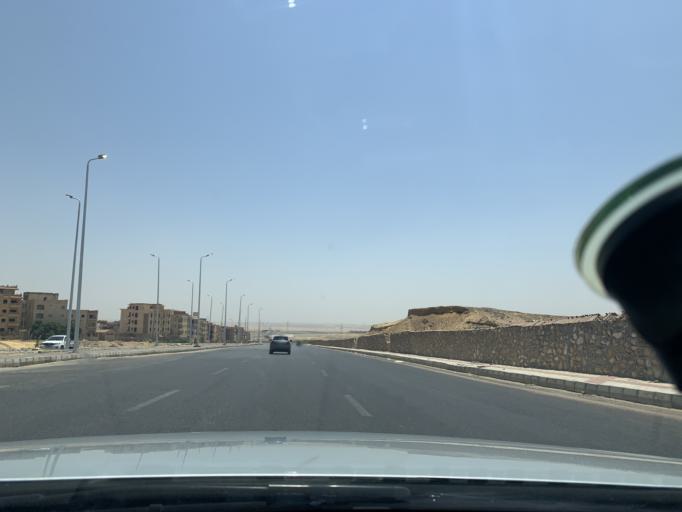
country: EG
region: Muhafazat al Qahirah
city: Halwan
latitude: 29.9860
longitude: 31.4686
